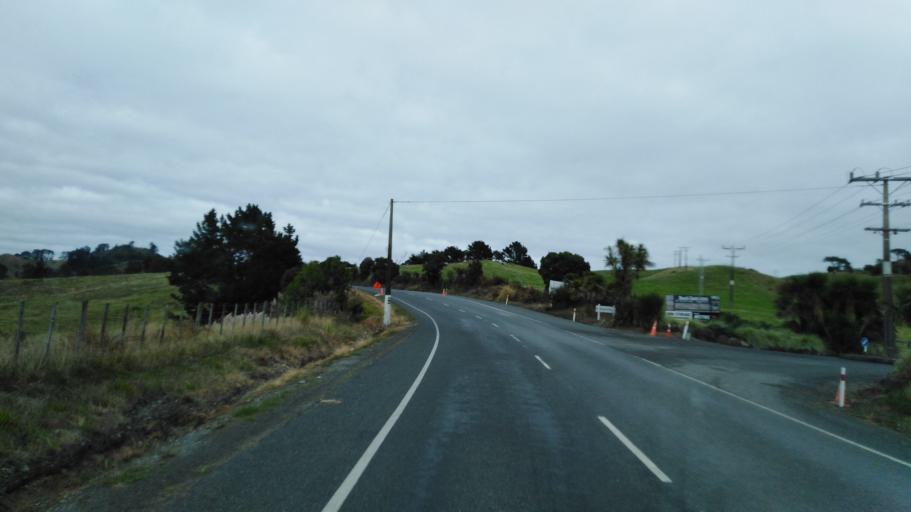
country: NZ
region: Bay of Plenty
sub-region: Western Bay of Plenty District
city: Waihi Beach
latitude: -37.4097
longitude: 175.9305
